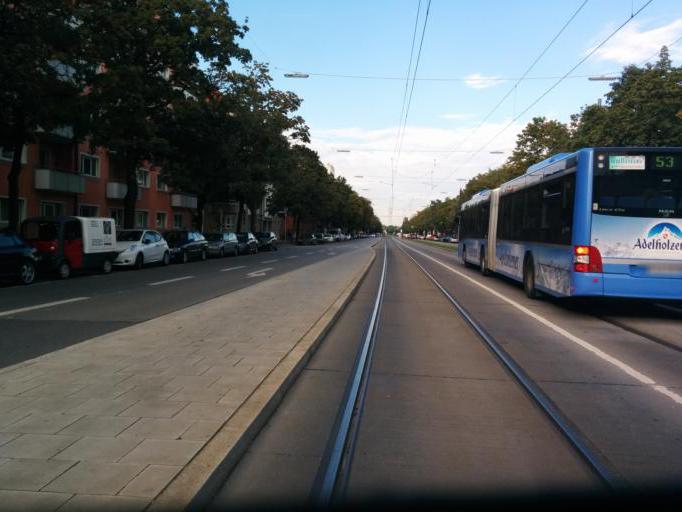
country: DE
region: Bavaria
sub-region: Upper Bavaria
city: Munich
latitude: 48.1557
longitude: 11.5404
